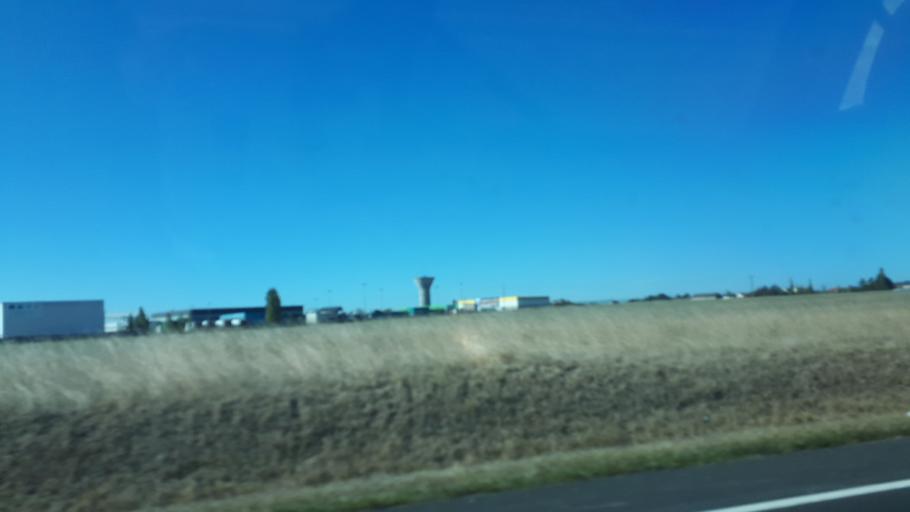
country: FR
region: Centre
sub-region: Departement d'Eure-et-Loir
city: Chateaudun
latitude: 48.0908
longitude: 1.3568
